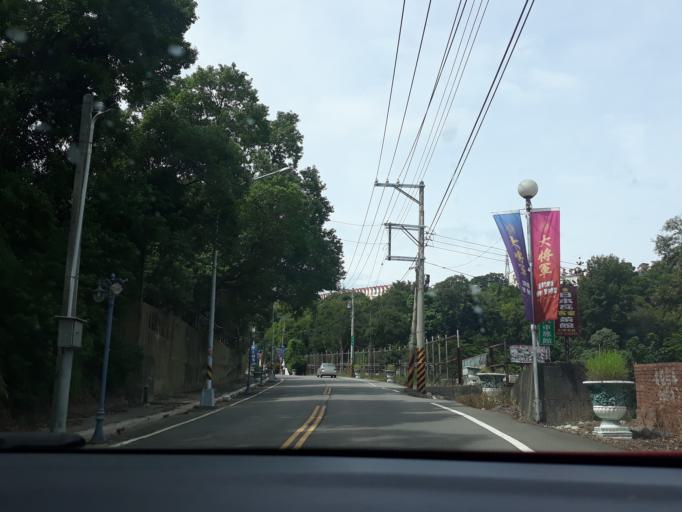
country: TW
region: Taiwan
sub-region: Miaoli
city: Miaoli
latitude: 24.5534
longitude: 120.8108
